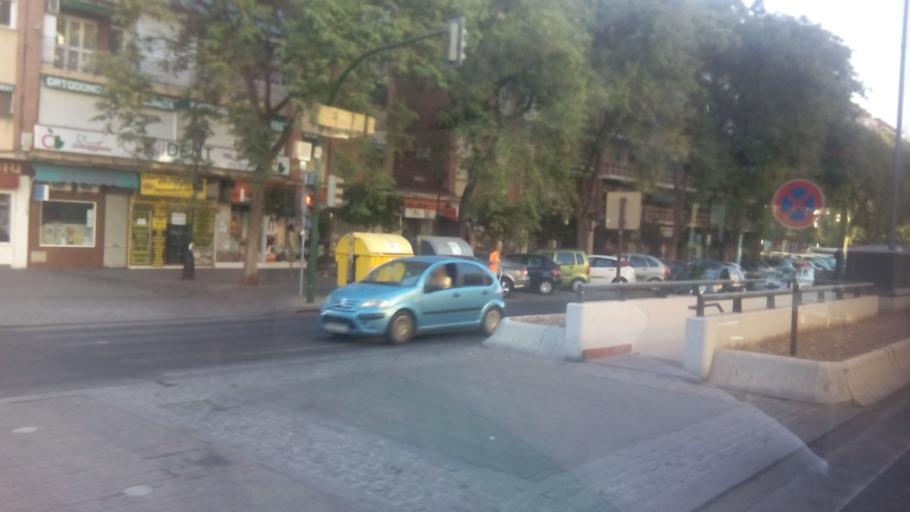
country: ES
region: Andalusia
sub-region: Province of Cordoba
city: Cordoba
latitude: 37.8901
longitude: -4.7646
